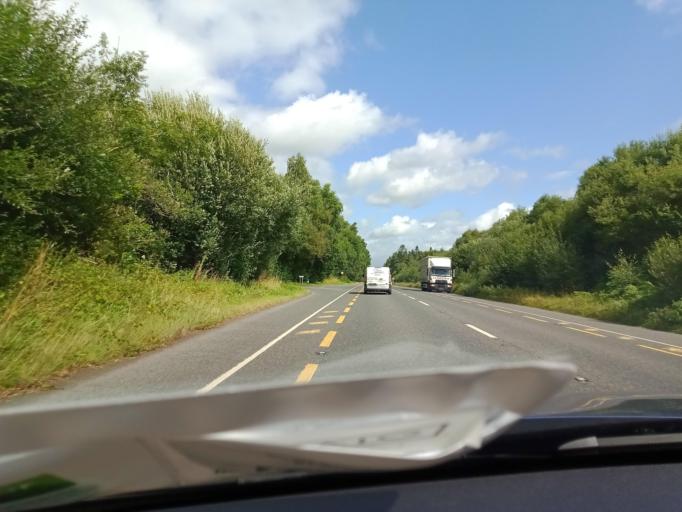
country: IE
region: Leinster
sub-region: Laois
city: Abbeyleix
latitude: 52.8963
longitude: -7.3602
